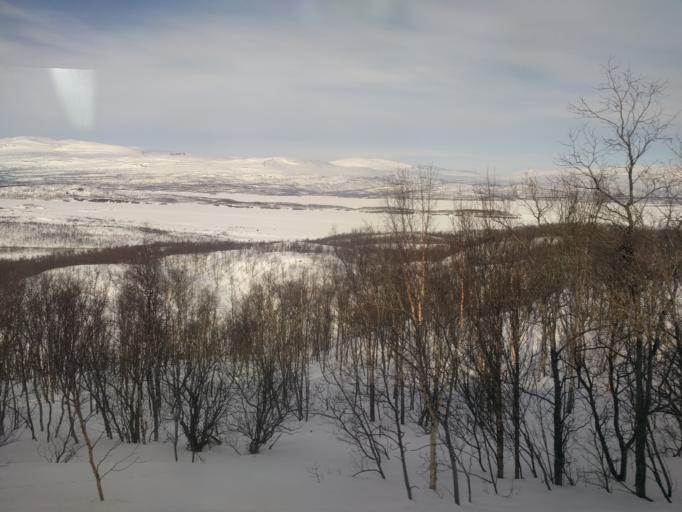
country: NO
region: Troms
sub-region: Bardu
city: Setermoen
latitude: 68.4286
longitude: 18.6478
